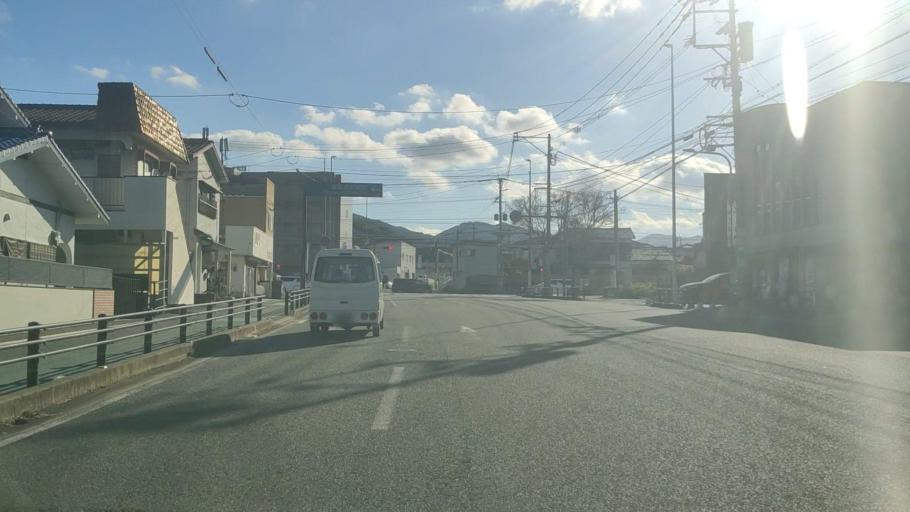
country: JP
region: Fukuoka
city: Fukuoka-shi
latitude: 33.5439
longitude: 130.3562
